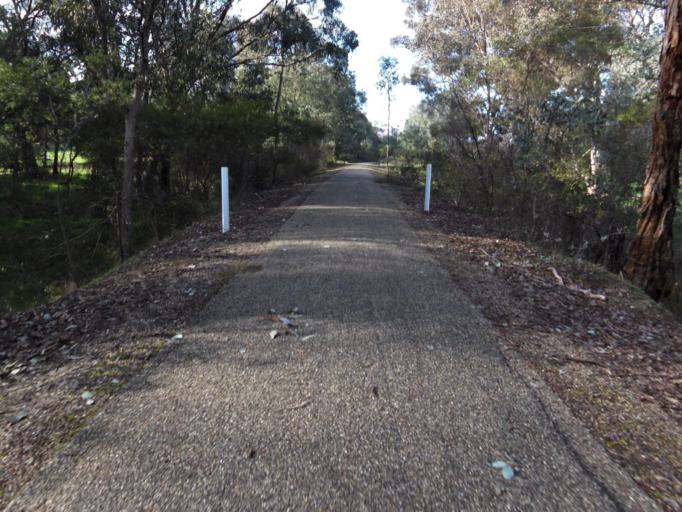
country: AU
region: Victoria
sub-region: Wangaratta
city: Wangaratta
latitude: -36.4086
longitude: 146.5479
